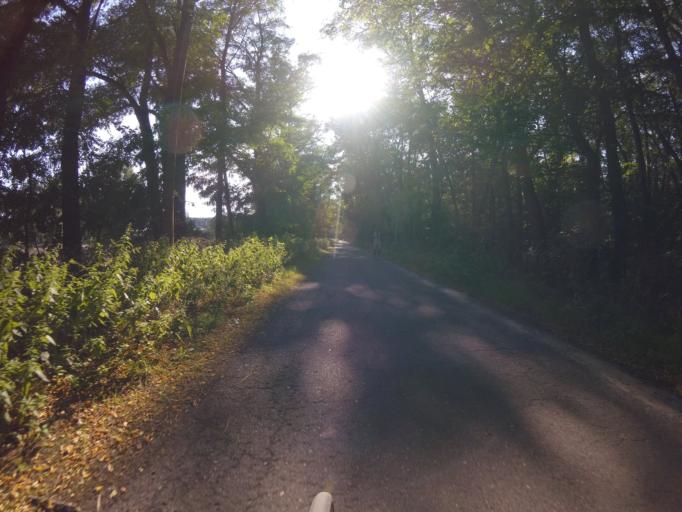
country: DE
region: Brandenburg
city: Bliesdorf
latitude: 52.6754
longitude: 14.1510
